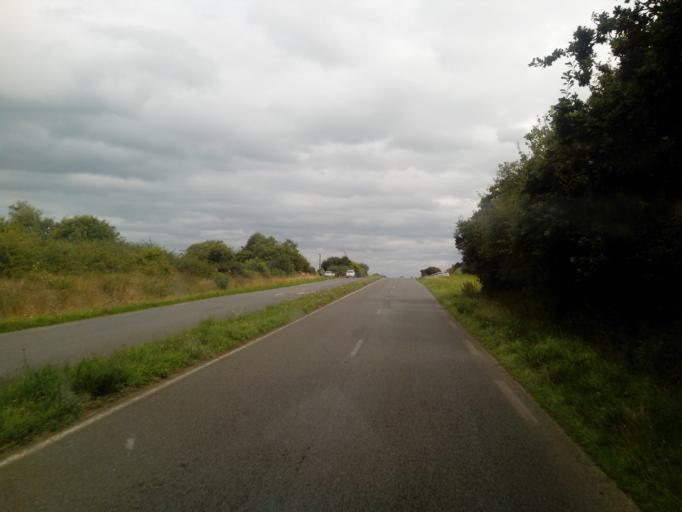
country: FR
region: Brittany
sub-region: Departement des Cotes-d'Armor
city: Saint-Quay-Portrieux
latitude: 48.6525
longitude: -2.8448
